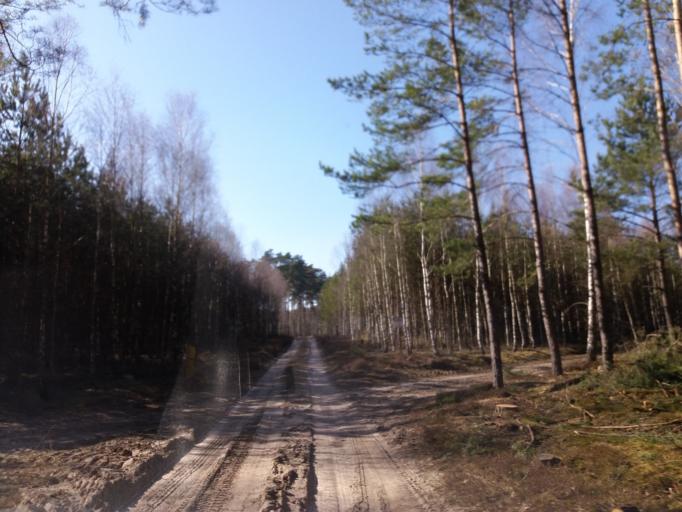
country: PL
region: West Pomeranian Voivodeship
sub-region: Powiat choszczenski
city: Bierzwnik
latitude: 53.1000
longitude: 15.7192
